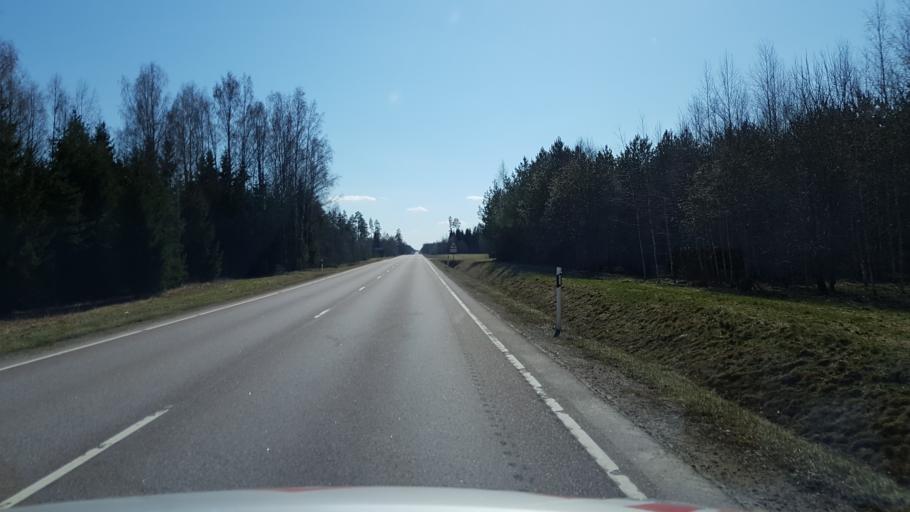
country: EE
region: Jogevamaa
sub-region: Mustvee linn
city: Mustvee
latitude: 58.7439
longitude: 26.8549
